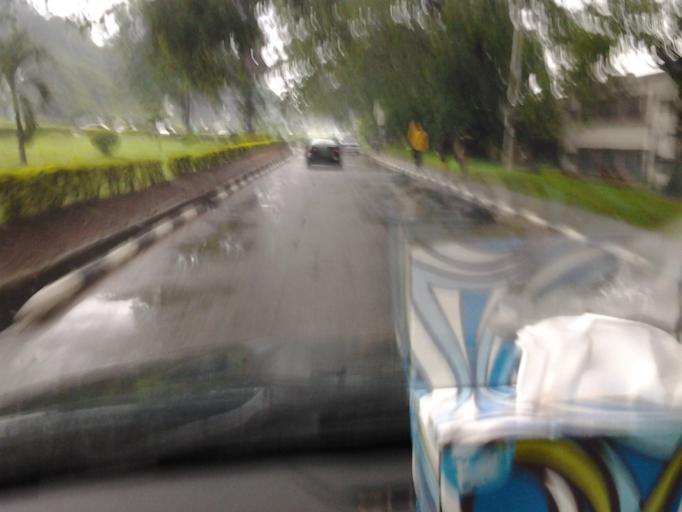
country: NG
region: Oyo
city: Ibadan
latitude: 7.4439
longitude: 3.9016
